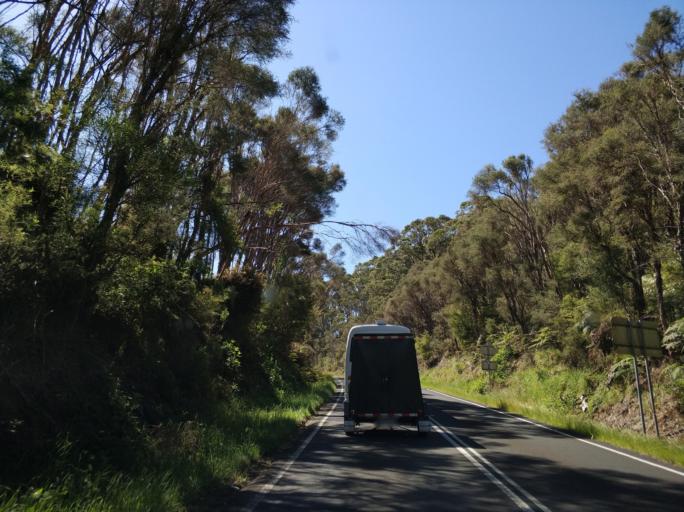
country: AU
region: Victoria
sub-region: Colac-Otway
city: Apollo Bay
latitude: -38.7252
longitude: 143.2481
